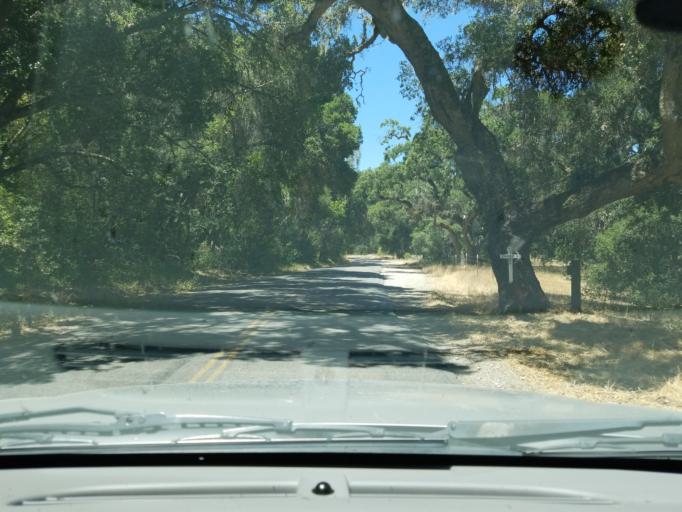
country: US
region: California
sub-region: Monterey County
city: Chualar
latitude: 36.4155
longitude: -121.5988
